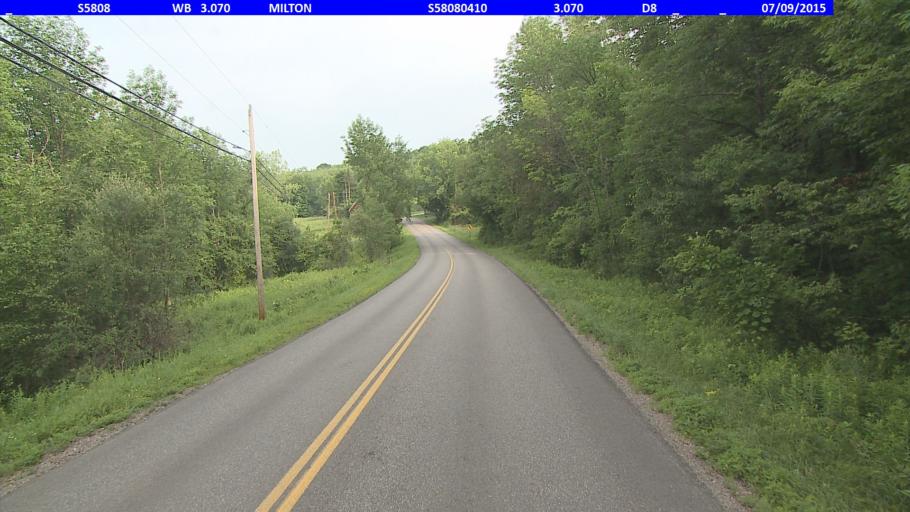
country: US
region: Vermont
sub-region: Chittenden County
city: Milton
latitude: 44.6418
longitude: -73.0580
